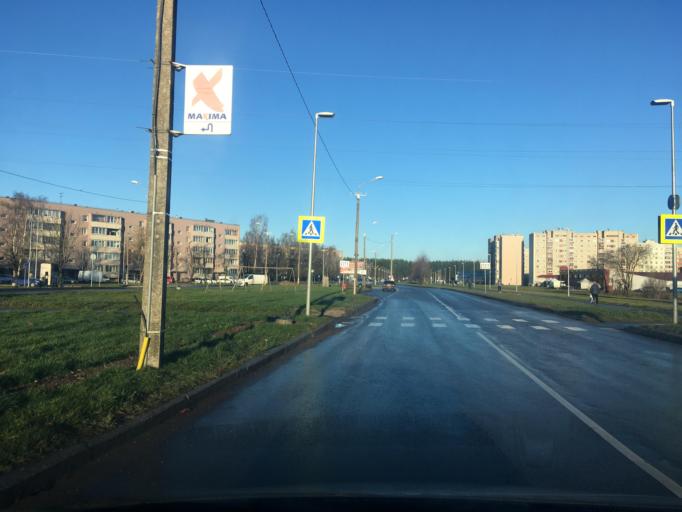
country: EE
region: Ida-Virumaa
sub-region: Narva linn
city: Narva
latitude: 59.3870
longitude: 28.1759
